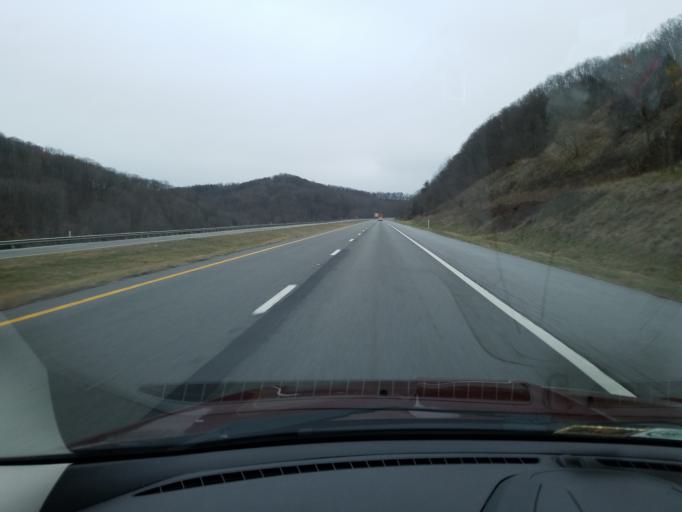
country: US
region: West Virginia
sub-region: Mercer County
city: Athens
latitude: 37.3412
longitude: -81.0048
